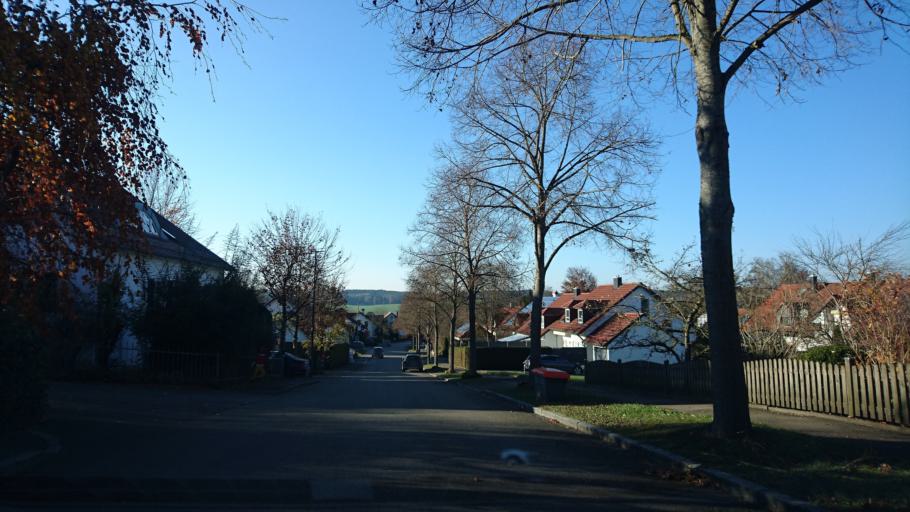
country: DE
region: Bavaria
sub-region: Swabia
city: Zusmarshausen
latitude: 48.3929
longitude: 10.6009
